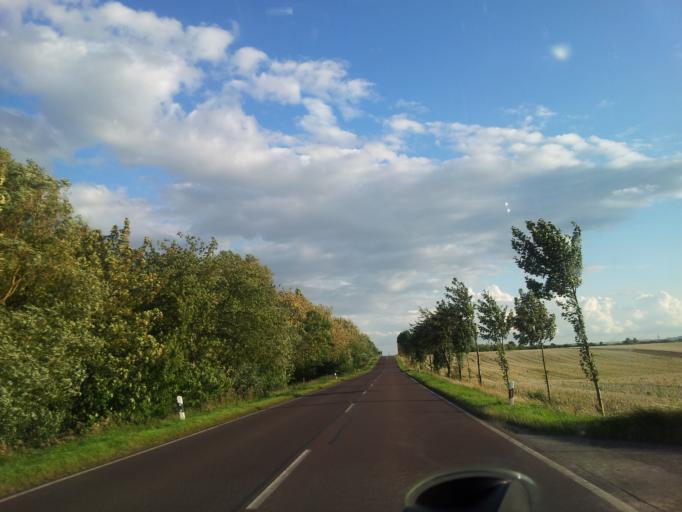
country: DE
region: Saxony-Anhalt
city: Aschersleben
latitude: 51.7876
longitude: 11.4589
